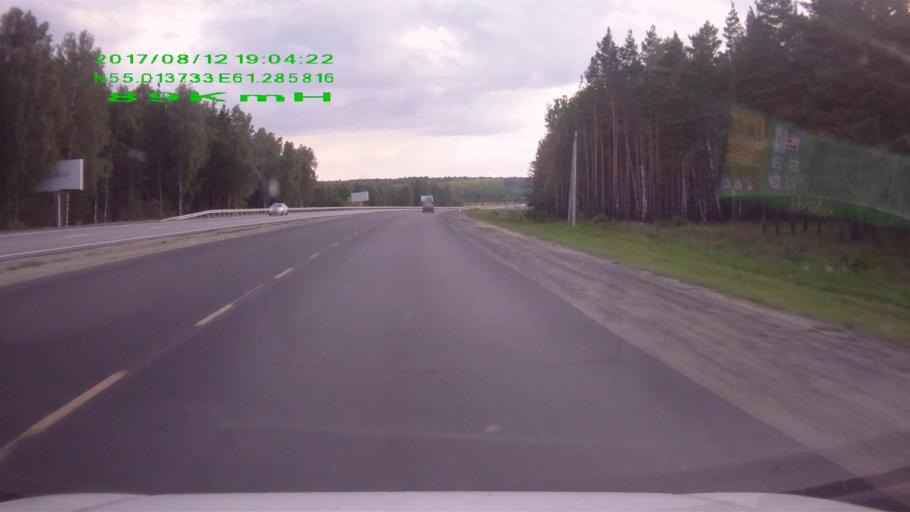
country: RU
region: Chelyabinsk
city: Sargazy
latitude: 55.0116
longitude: 61.2686
